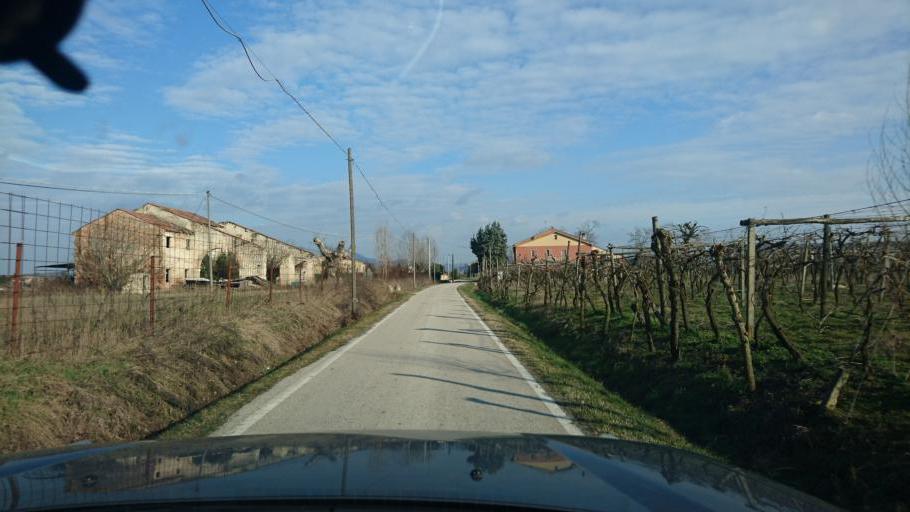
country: IT
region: Veneto
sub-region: Provincia di Vicenza
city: Sossano
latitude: 45.3558
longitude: 11.5250
